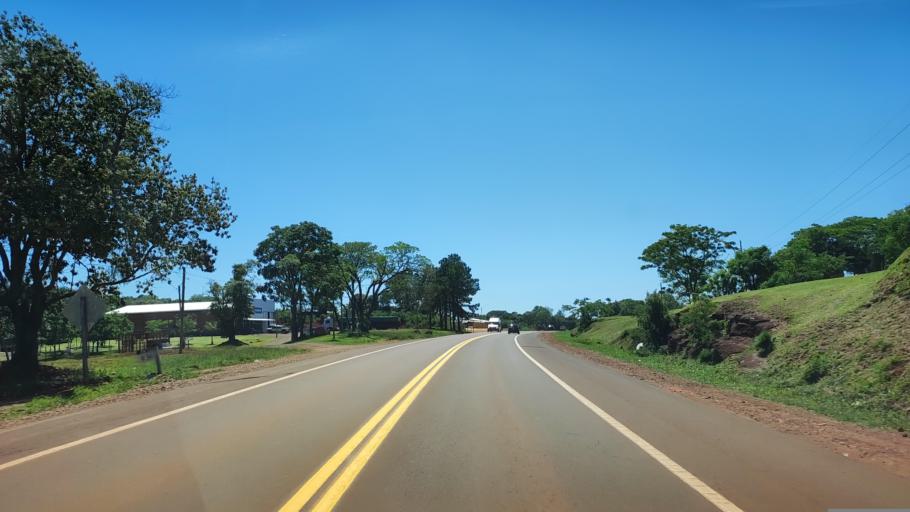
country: AR
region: Misiones
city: Aristobulo del Valle
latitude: -27.0834
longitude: -54.8161
